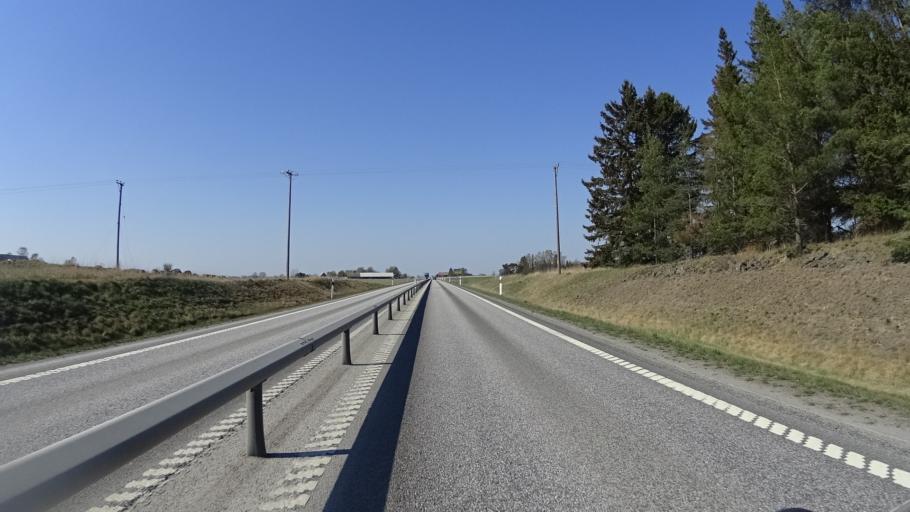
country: SE
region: OEstergoetland
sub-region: Linkopings Kommun
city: Malmslatt
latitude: 58.3272
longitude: 15.5643
